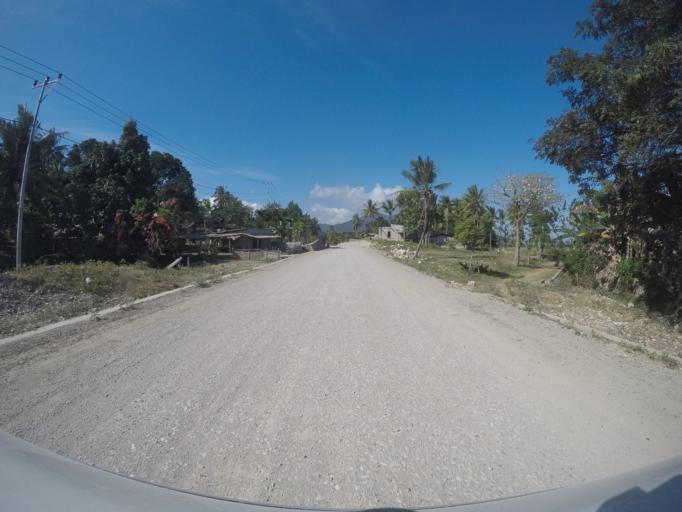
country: TL
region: Viqueque
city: Viqueque
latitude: -8.8147
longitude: 126.5358
